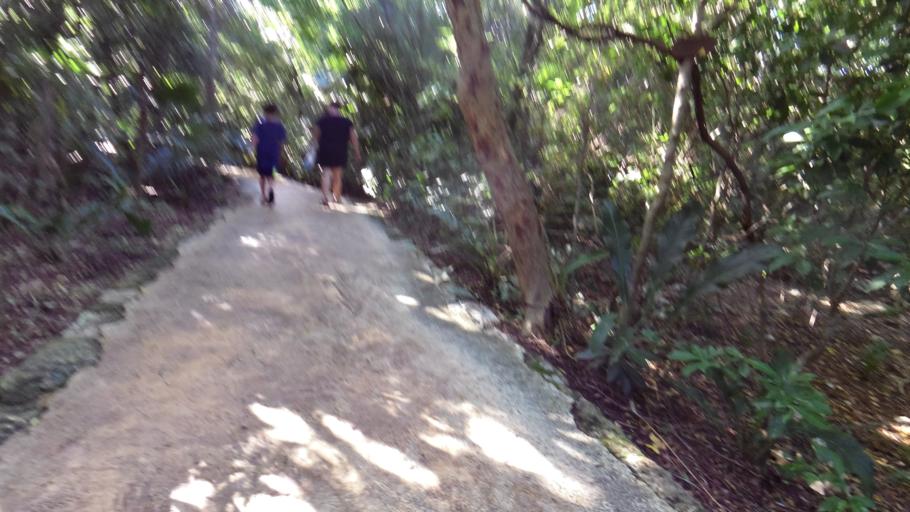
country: MX
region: Quintana Roo
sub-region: Tulum
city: Ciudad Chemuyil
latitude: 20.3181
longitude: -87.3597
